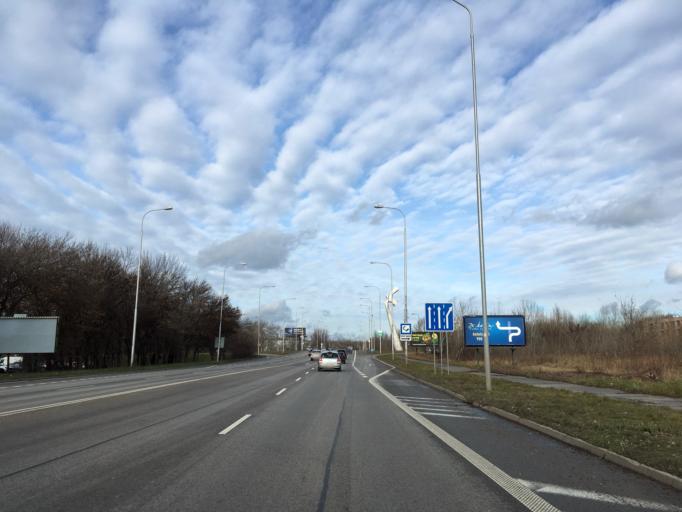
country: SK
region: Bratislavsky
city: Bratislava
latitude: 48.0970
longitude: 17.1211
